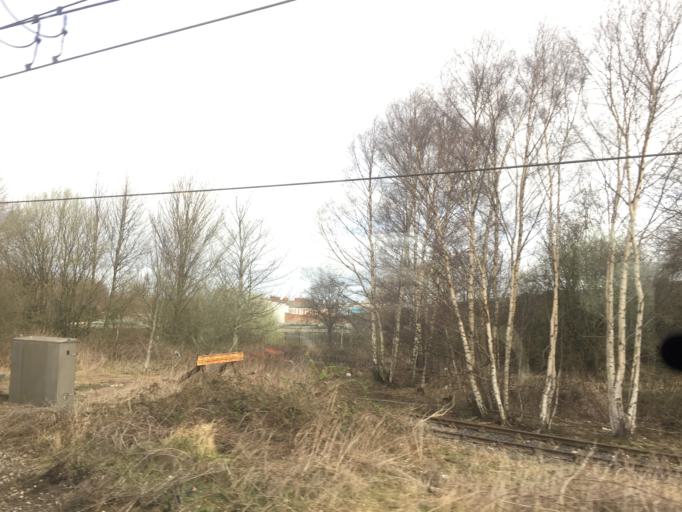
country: GB
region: England
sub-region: Cumbria
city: Carlisle
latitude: 54.8853
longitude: -2.9265
